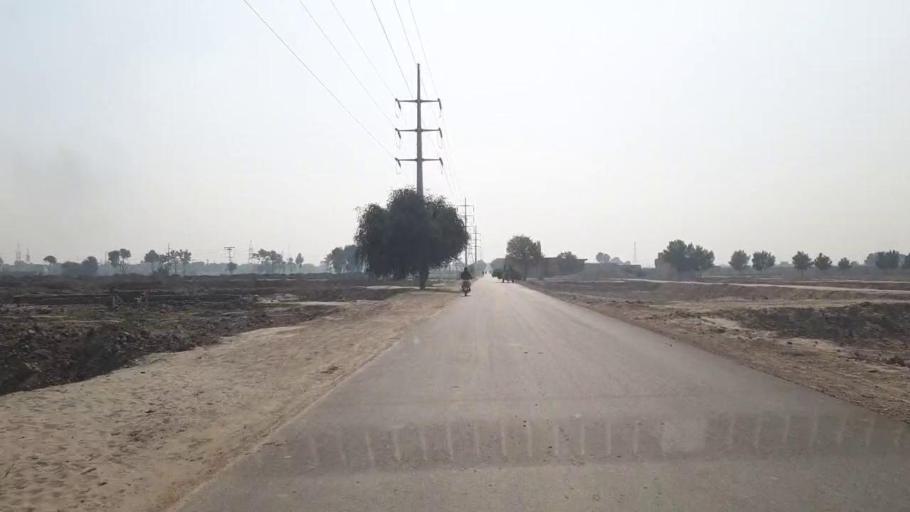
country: PK
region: Sindh
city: Hala
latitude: 25.8292
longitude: 68.4198
